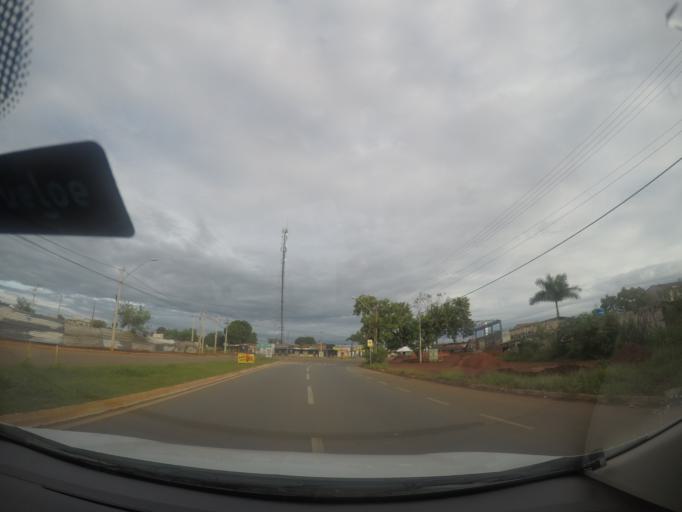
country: BR
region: Goias
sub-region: Goiania
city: Goiania
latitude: -16.6246
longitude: -49.3358
